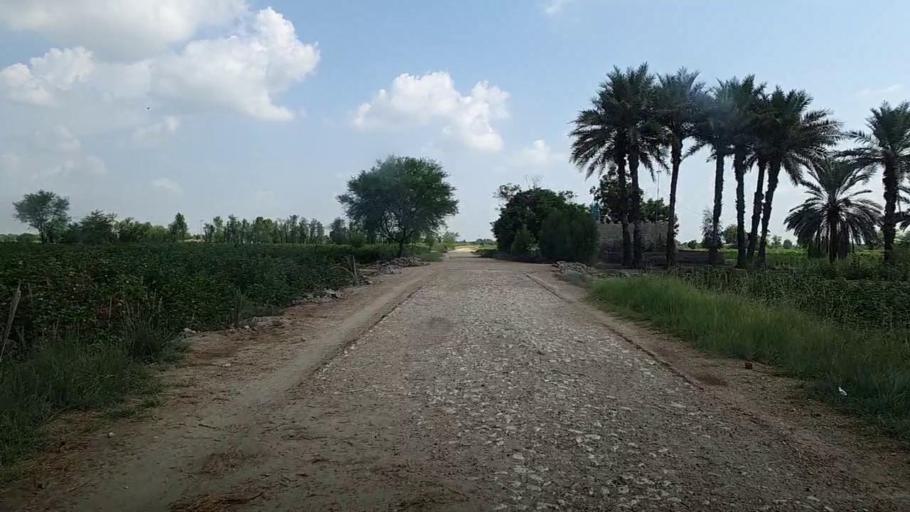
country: PK
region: Sindh
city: Kandiaro
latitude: 26.9898
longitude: 68.3053
